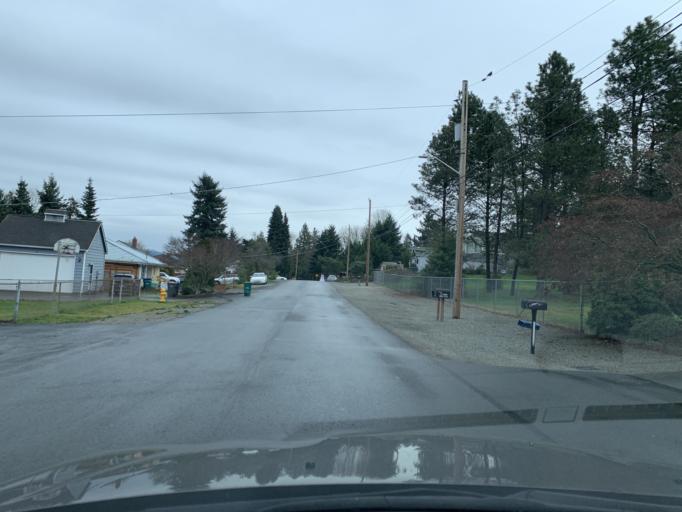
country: US
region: Washington
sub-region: King County
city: SeaTac
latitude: 47.4621
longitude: -122.2774
